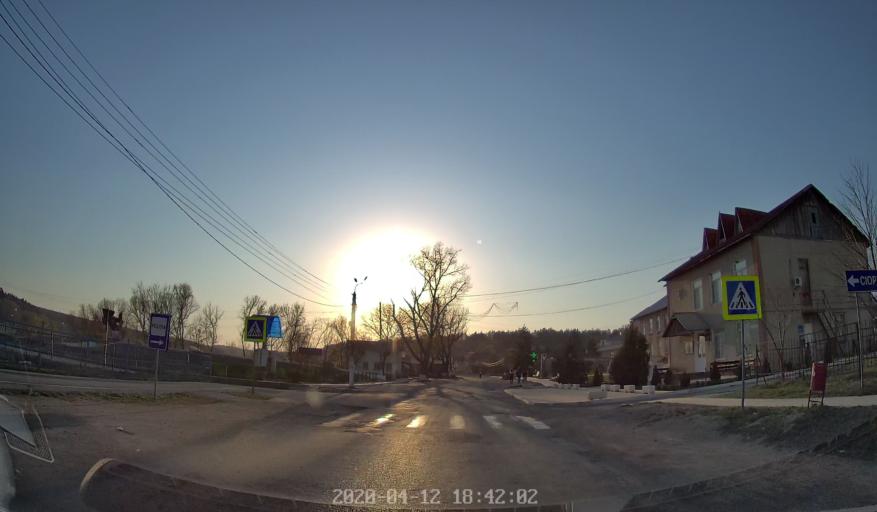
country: MD
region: Chisinau
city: Ciorescu
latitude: 47.1357
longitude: 28.9426
